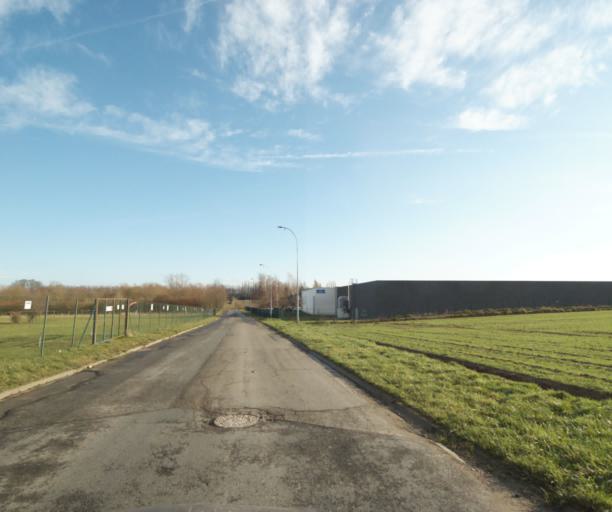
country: FR
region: Nord-Pas-de-Calais
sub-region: Departement du Nord
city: Marly
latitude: 50.3487
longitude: 3.5647
